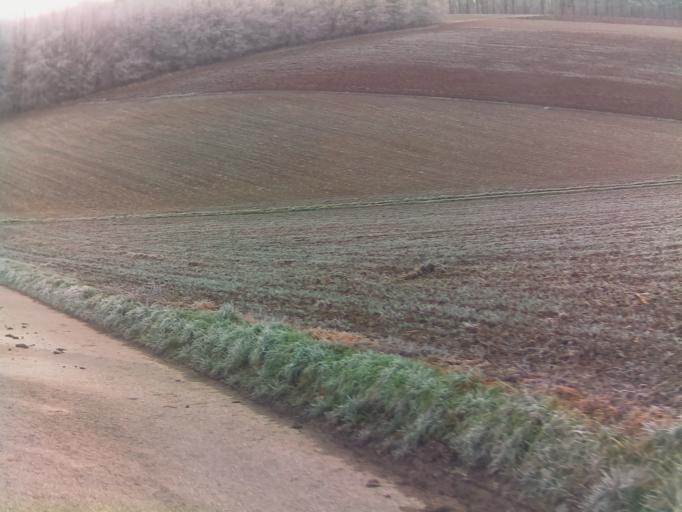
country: DE
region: Baden-Wuerttemberg
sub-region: Regierungsbezirk Stuttgart
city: Boxberg
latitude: 49.5136
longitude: 9.6322
